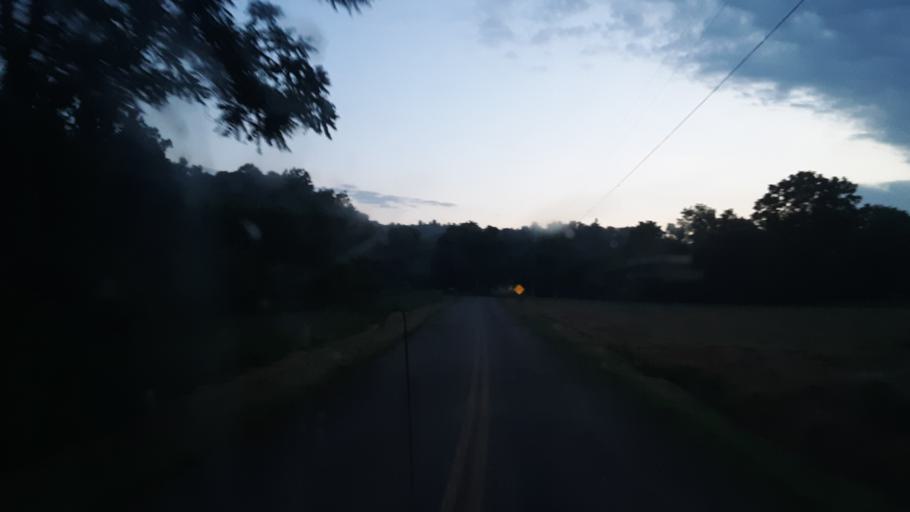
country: US
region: Ohio
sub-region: Carroll County
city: Carrollton
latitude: 40.5939
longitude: -81.1161
